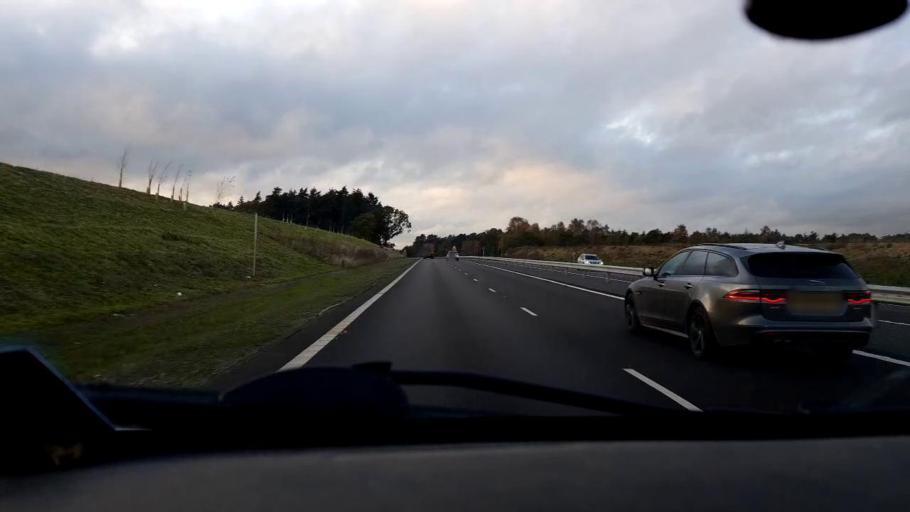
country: GB
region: England
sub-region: Norfolk
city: Horsford
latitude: 52.6945
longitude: 1.2211
